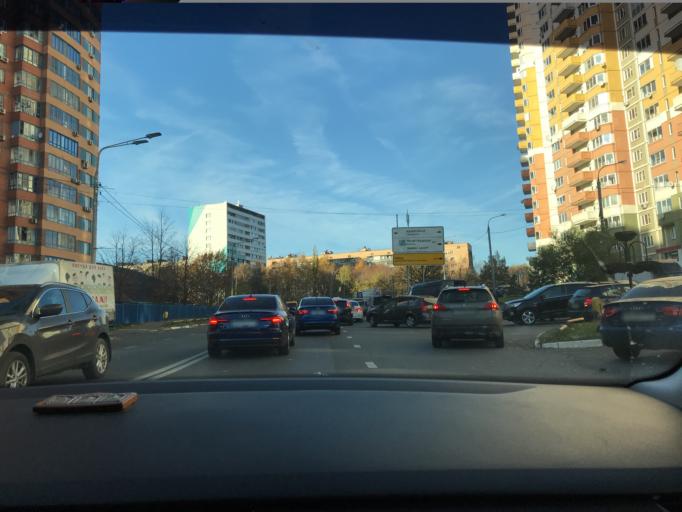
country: RU
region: Moscow
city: Khimki
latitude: 55.8857
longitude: 37.4268
